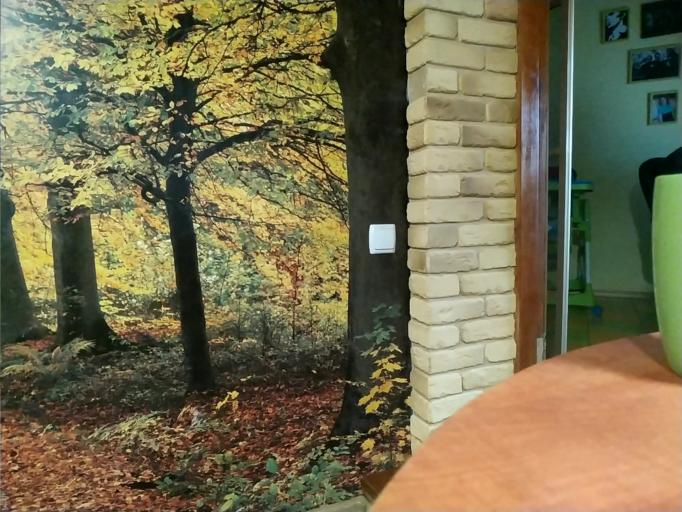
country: RU
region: Tverskaya
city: Staraya Toropa
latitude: 56.3455
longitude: 31.8339
